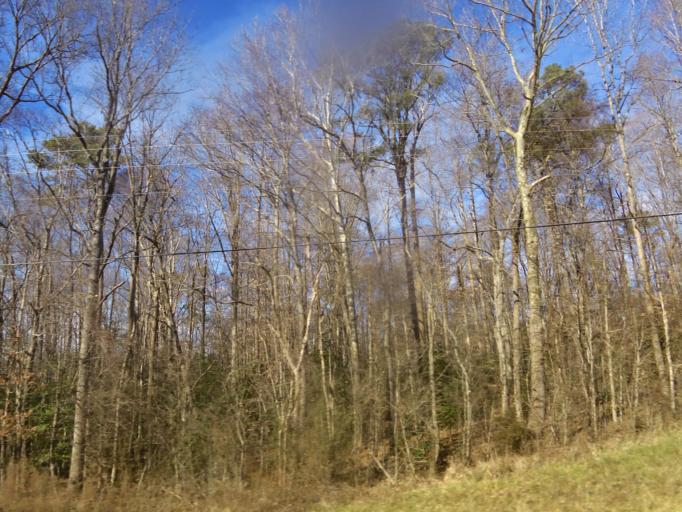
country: US
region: Virginia
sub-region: Isle of Wight County
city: Windsor
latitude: 36.7812
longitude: -76.8297
